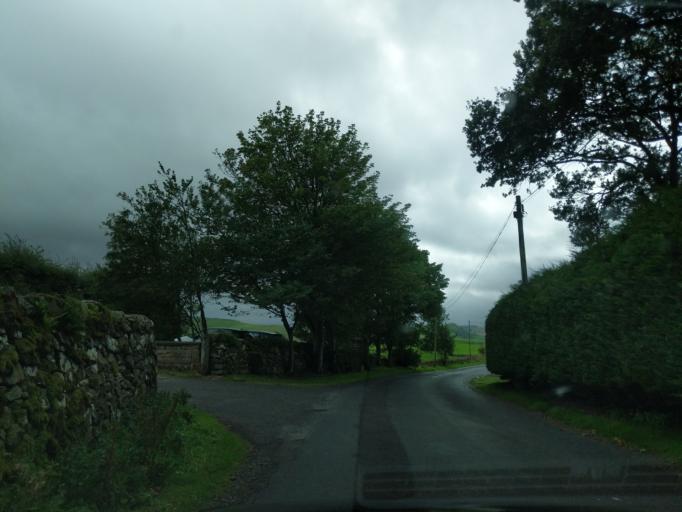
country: GB
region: Scotland
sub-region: The Scottish Borders
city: Kelso
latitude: 55.6650
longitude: -2.4727
